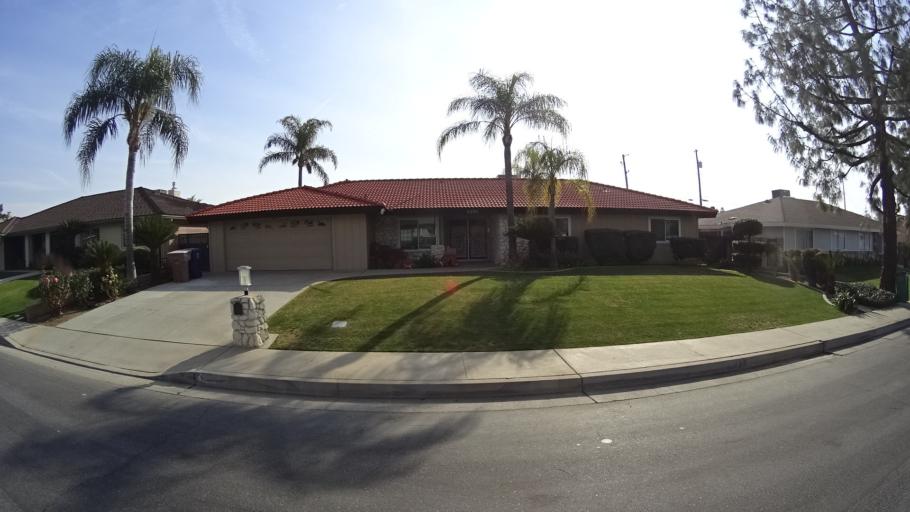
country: US
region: California
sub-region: Kern County
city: Oildale
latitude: 35.4076
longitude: -118.9454
